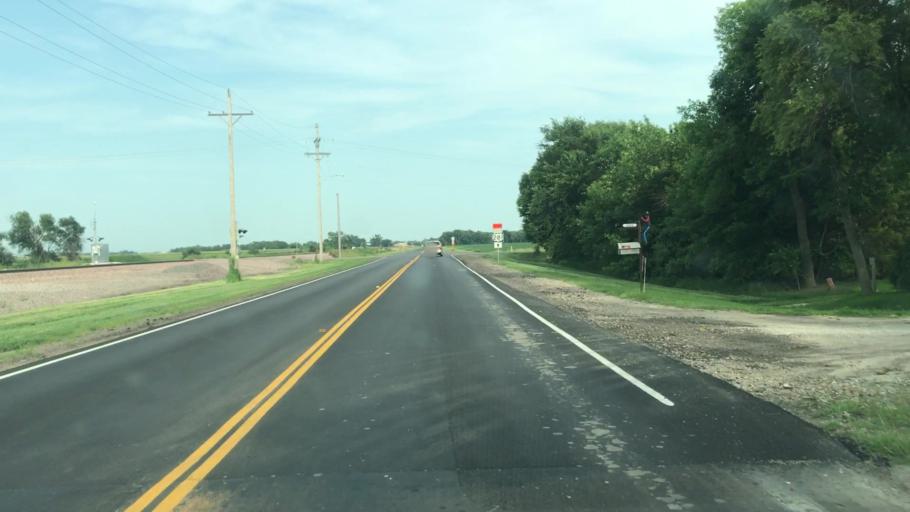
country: US
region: Nebraska
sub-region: Hall County
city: Grand Island
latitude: 40.9527
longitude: -98.3801
